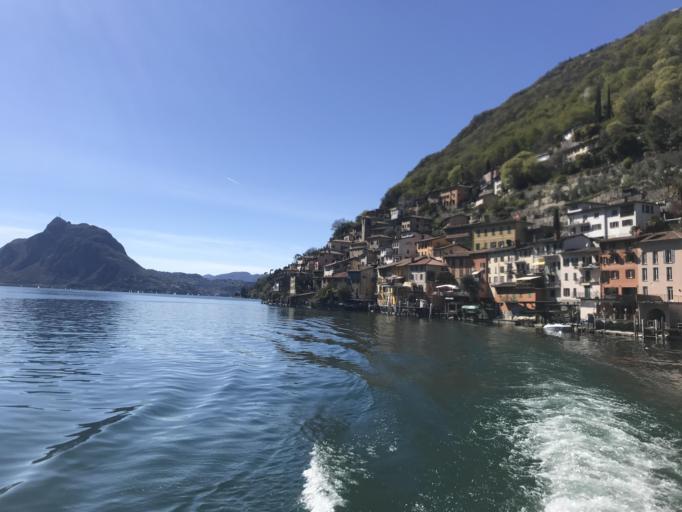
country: IT
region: Lombardy
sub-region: Provincia di Como
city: Lanzo d'Intelvi
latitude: 46.0057
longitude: 9.0059
